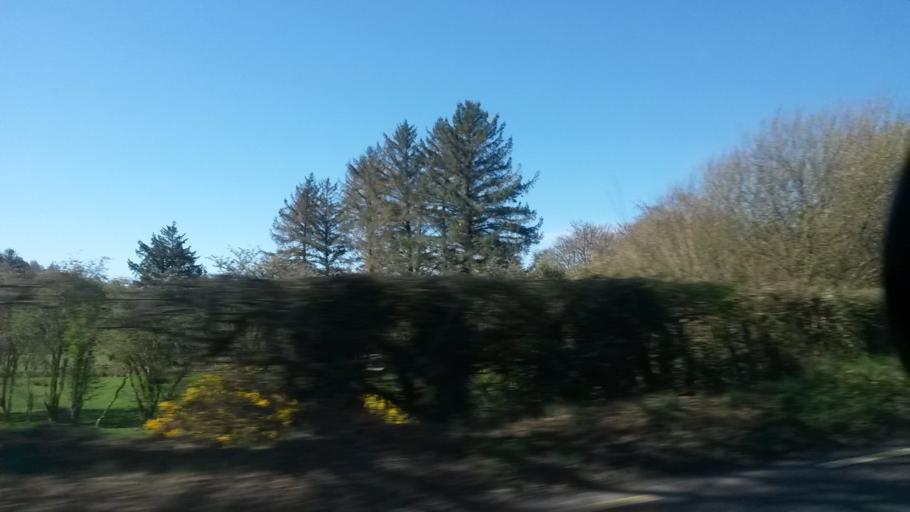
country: IE
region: Munster
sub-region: County Cork
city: Millstreet
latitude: 51.9463
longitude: -9.1747
